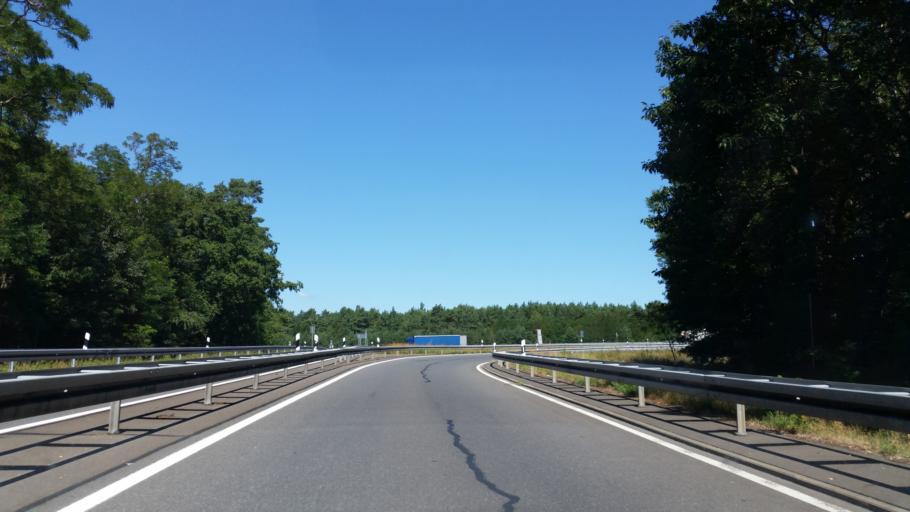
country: DE
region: Brandenburg
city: Cottbus
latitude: 51.7234
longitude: 14.2980
